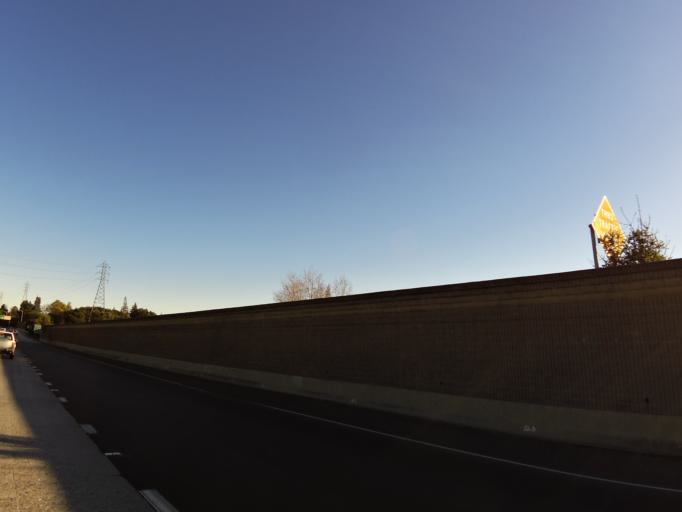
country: US
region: California
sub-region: Santa Clara County
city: Cupertino
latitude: 37.3337
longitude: -122.0643
